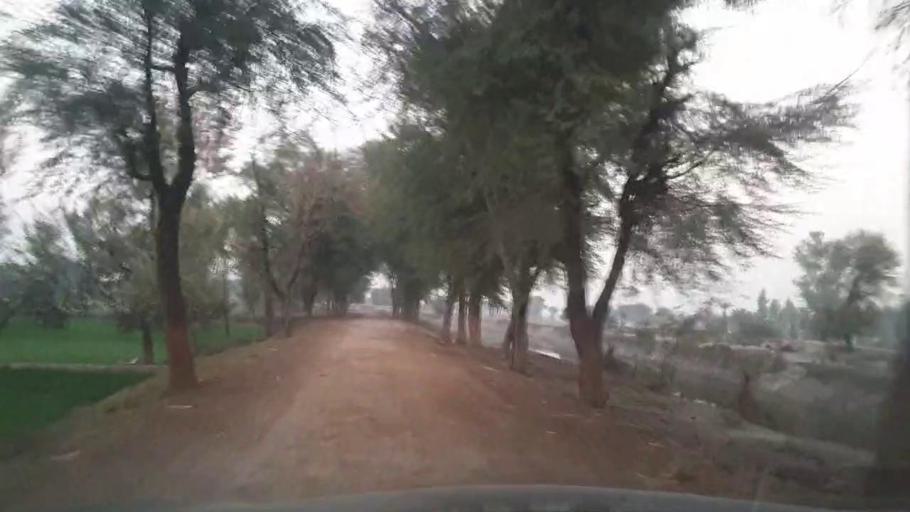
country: PK
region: Sindh
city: Ubauro
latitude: 28.1826
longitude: 69.7809
